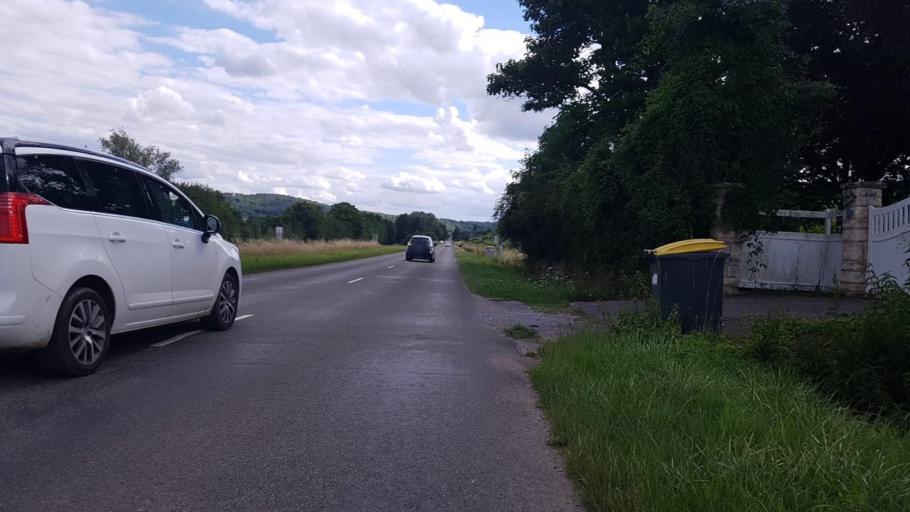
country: FR
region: Picardie
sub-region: Departement de l'Aisne
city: Crezancy
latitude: 49.0660
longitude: 3.4797
